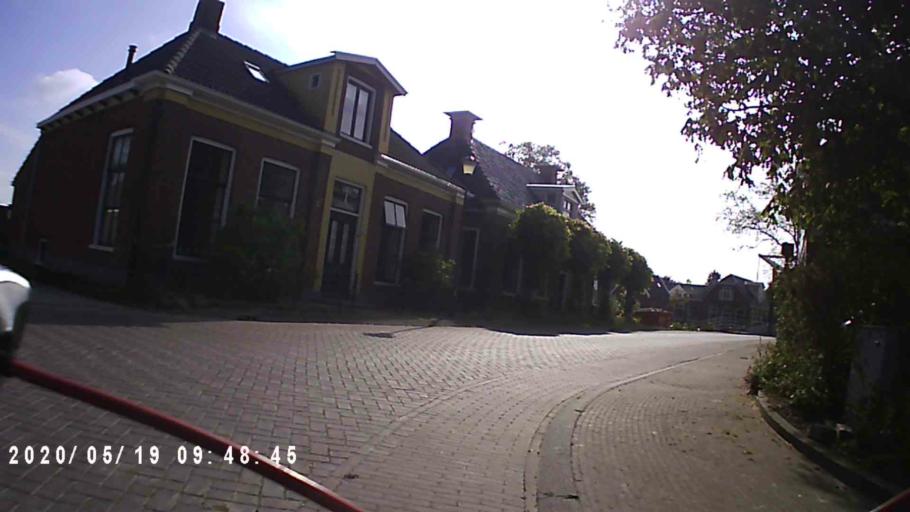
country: NL
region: Groningen
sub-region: Gemeente Zuidhorn
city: Grijpskerk
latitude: 53.2817
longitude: 6.2675
